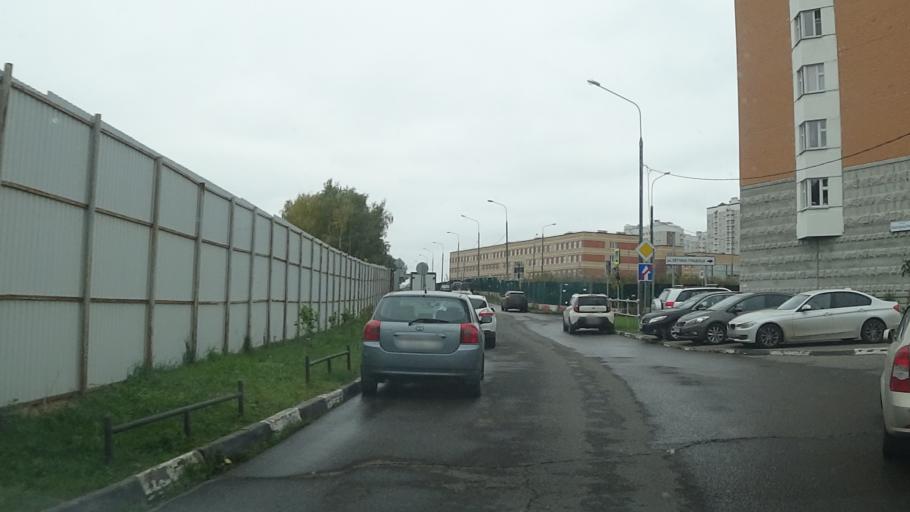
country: RU
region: Moskovskaya
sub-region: Leninskiy Rayon
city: Vnukovo
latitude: 55.6230
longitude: 37.3137
